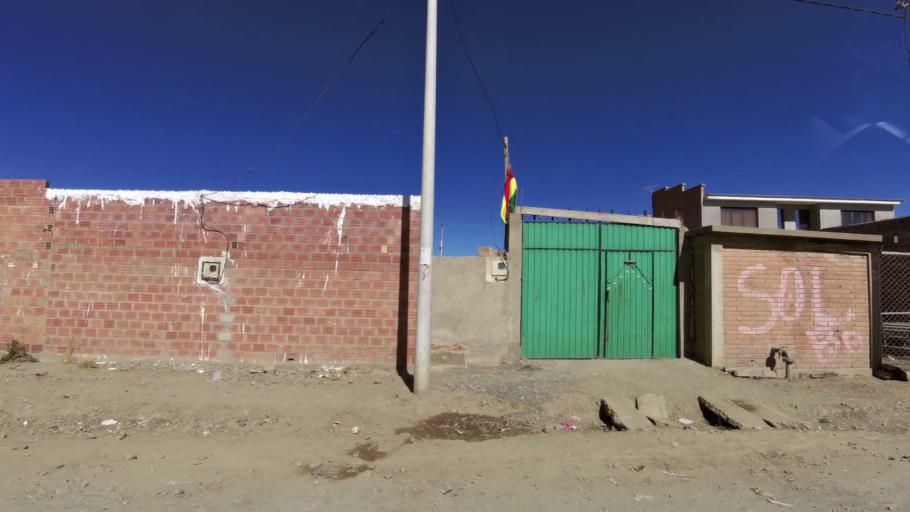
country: BO
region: La Paz
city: La Paz
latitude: -16.6086
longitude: -68.1979
